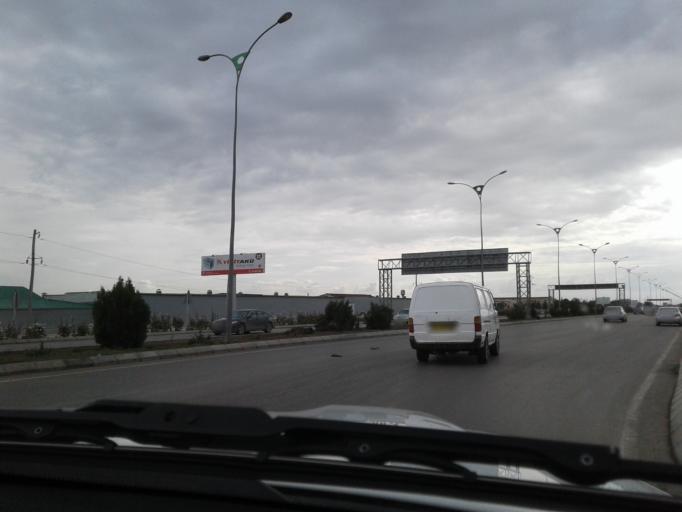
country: TM
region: Mary
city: Mary
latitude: 37.5930
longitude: 61.8149
